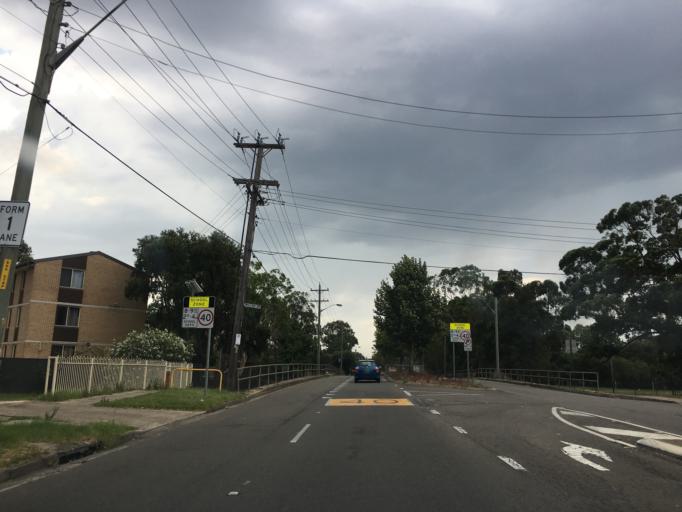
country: AU
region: New South Wales
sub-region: Liverpool
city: Miller
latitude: -33.9268
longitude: 150.8904
